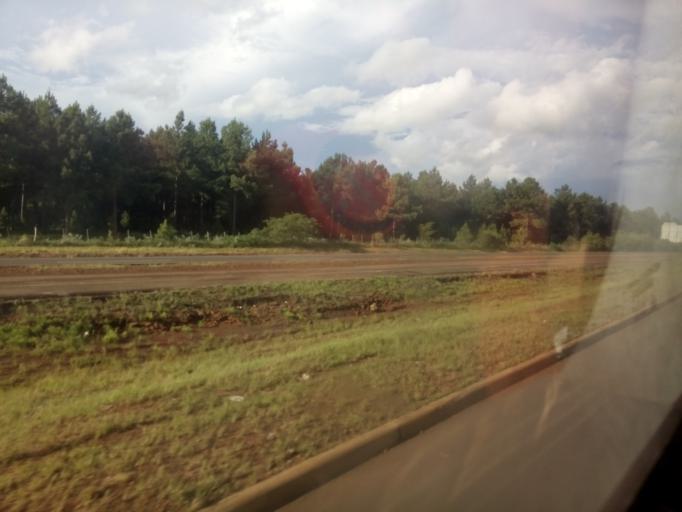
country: AR
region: Misiones
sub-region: Departamento de Candelaria
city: Candelaria
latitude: -27.4619
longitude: -55.6787
